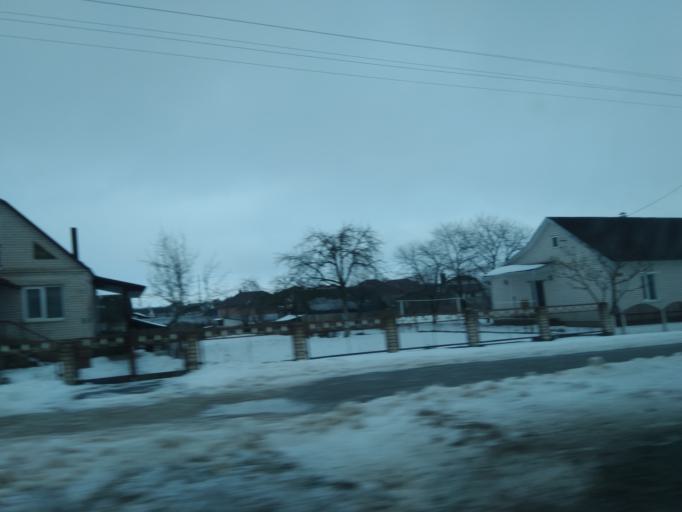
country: BY
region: Minsk
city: Nyasvizh
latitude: 53.2278
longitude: 26.6642
